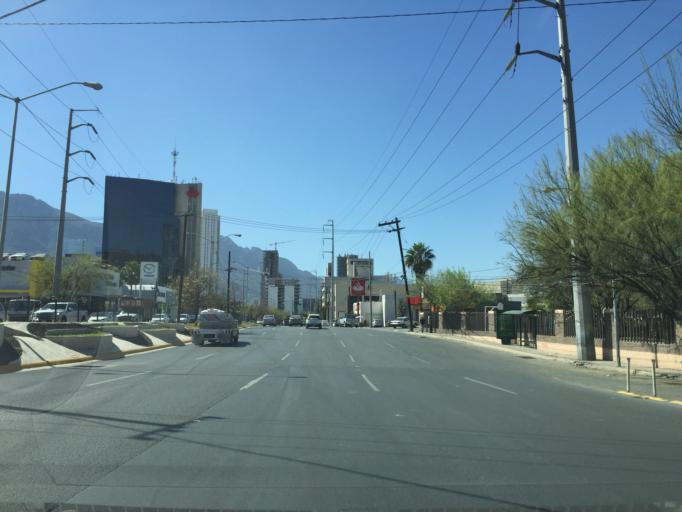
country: MX
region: Nuevo Leon
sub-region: Monterrey
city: Monterrey
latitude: 25.6539
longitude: -100.3412
